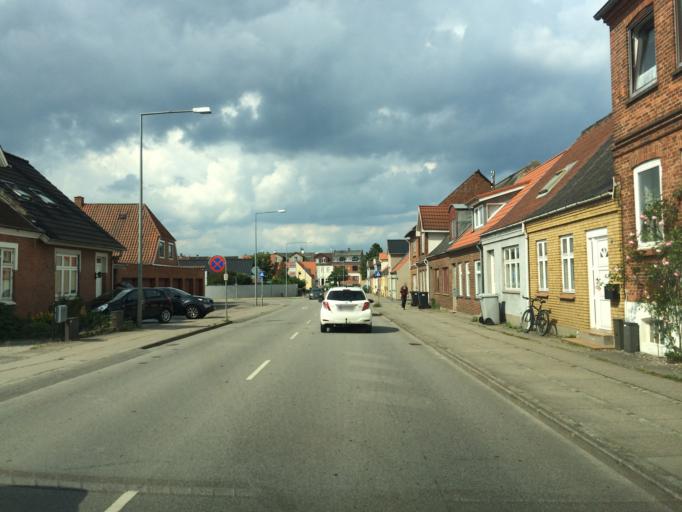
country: DK
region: South Denmark
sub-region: Middelfart Kommune
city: Middelfart
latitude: 55.5019
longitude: 9.7399
